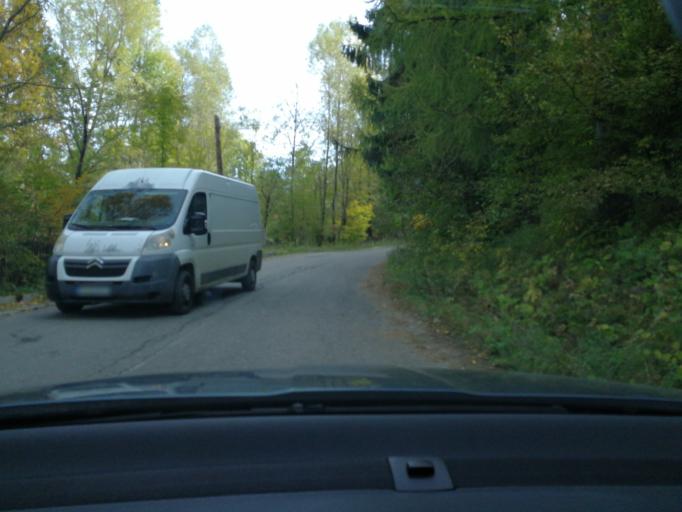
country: RO
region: Prahova
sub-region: Comuna Brebu
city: Pietriceaua
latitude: 45.2049
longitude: 25.8004
